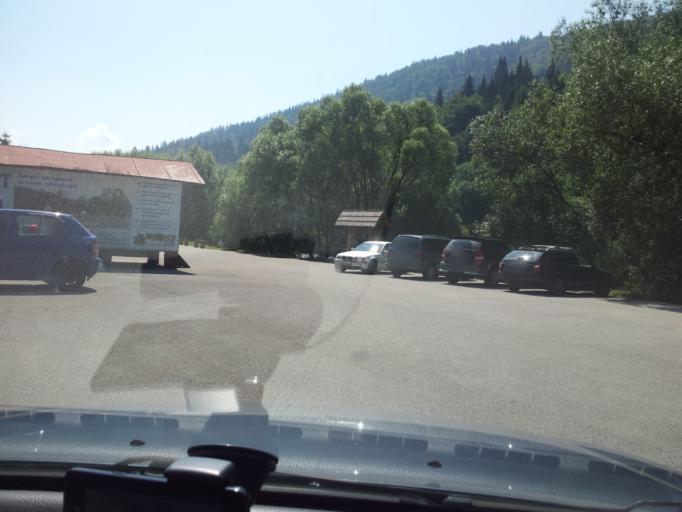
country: SK
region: Zilinsky
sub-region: Okres Dolny Kubin
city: Dolny Kubin
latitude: 49.2562
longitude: 19.3940
